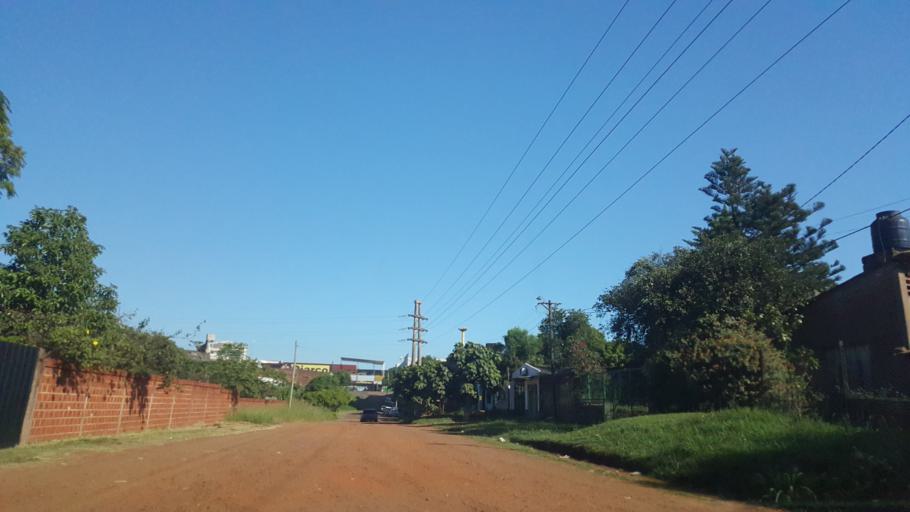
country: AR
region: Misiones
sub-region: Departamento de Capital
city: Posadas
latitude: -27.4058
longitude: -55.9006
